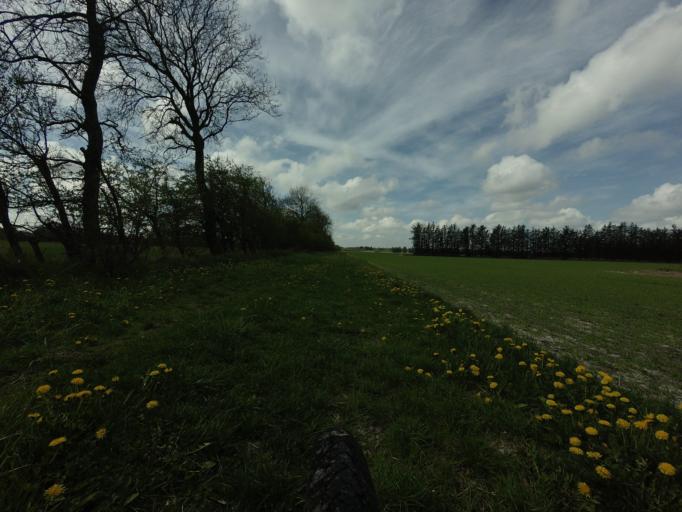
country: DK
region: North Denmark
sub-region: Jammerbugt Kommune
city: Kas
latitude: 57.1960
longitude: 9.6157
